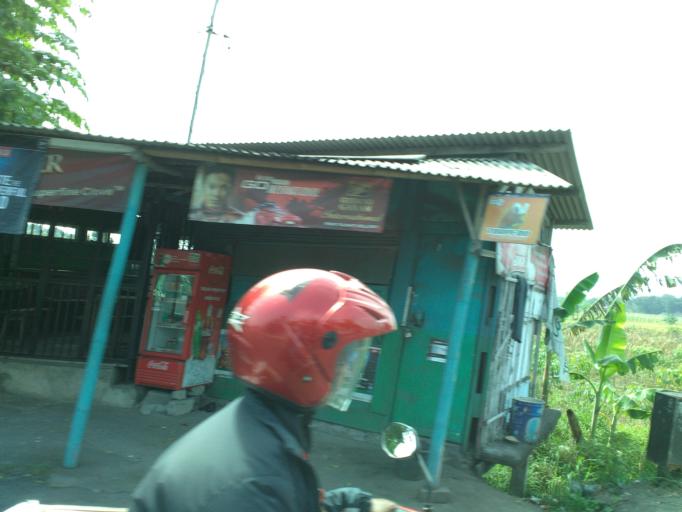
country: ID
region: Central Java
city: Candi Prambanan
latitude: -7.7472
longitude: 110.5244
